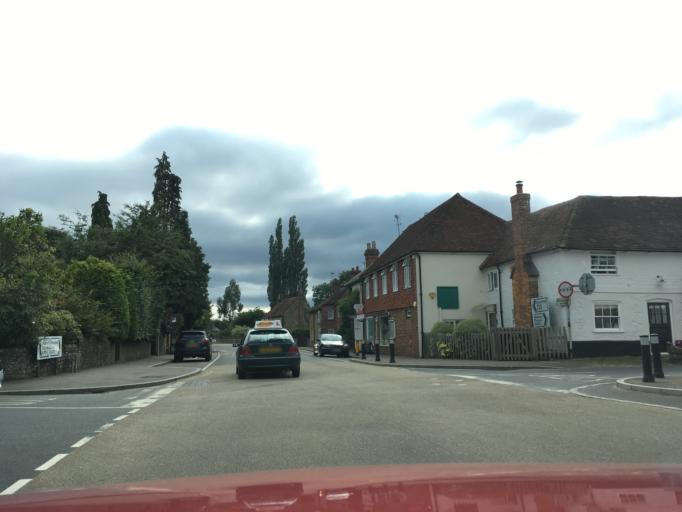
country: GB
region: England
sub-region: West Sussex
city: Milland
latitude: 51.0081
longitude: -0.8505
